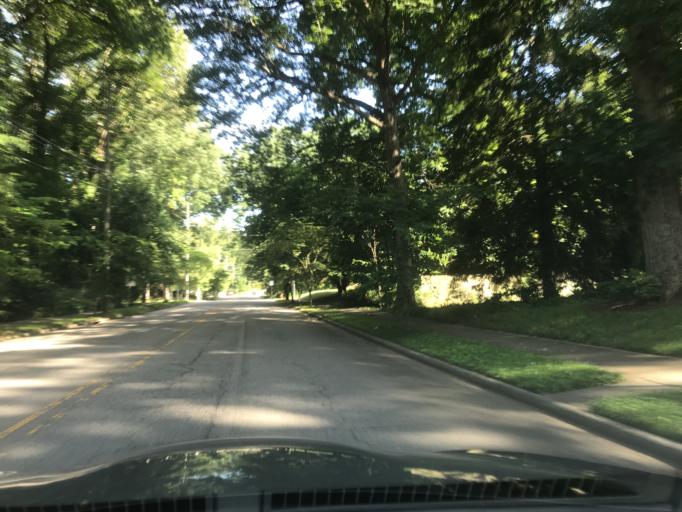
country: US
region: North Carolina
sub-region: Wake County
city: Raleigh
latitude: 35.8259
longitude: -78.6003
